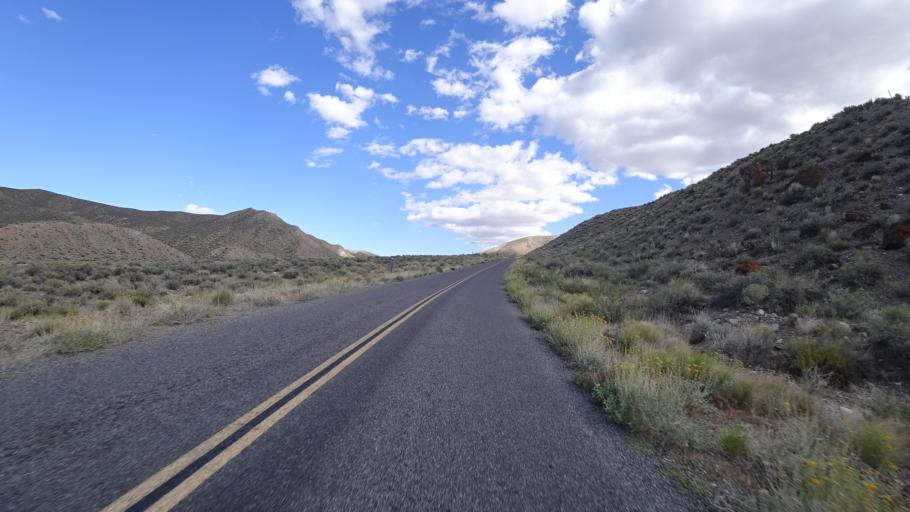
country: US
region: Nevada
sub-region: Nye County
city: Beatty
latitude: 36.4132
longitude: -117.1774
